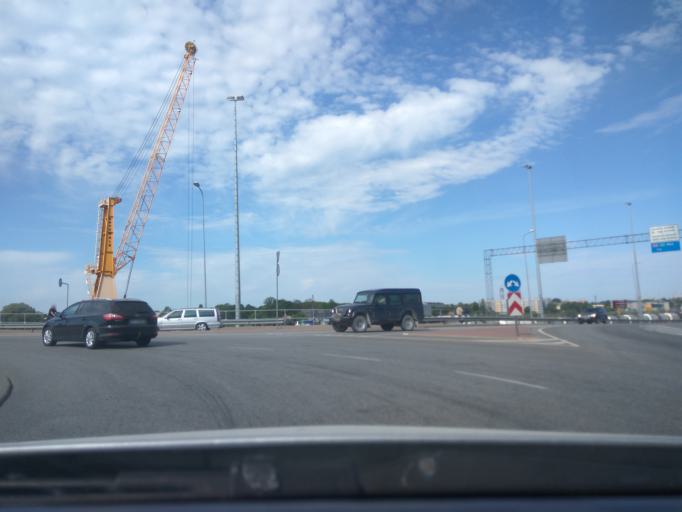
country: LV
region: Ventspils
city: Ventspils
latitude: 57.3900
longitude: 21.5910
